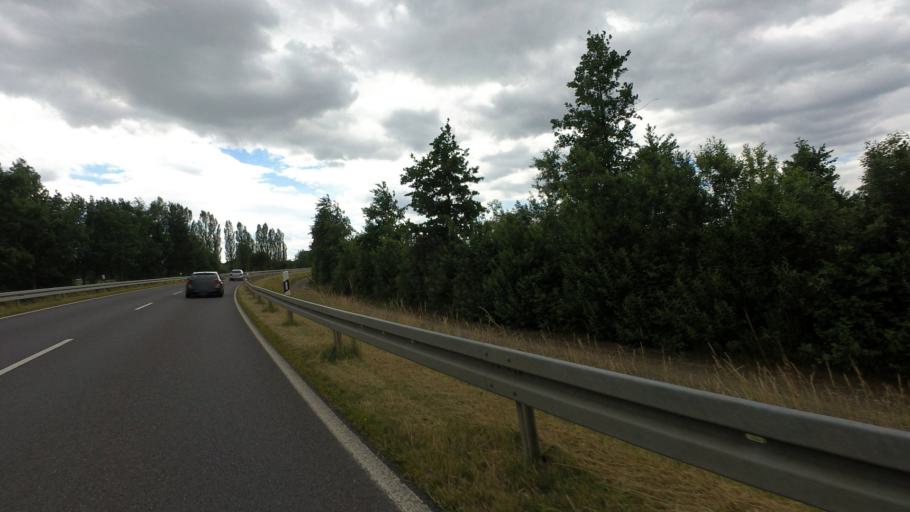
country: DE
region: Saxony
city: Wittichenau
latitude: 51.3864
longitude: 14.2330
